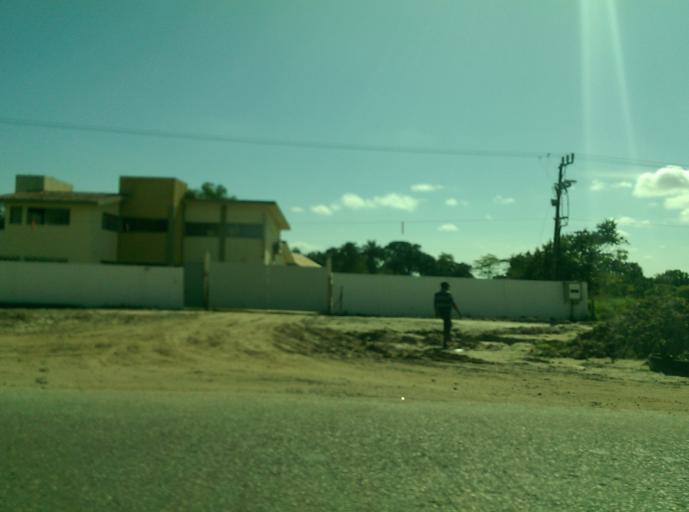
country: MX
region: Tabasco
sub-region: Centro
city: Anacleto Canabal 2da. Seccion
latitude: 17.9821
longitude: -93.0218
